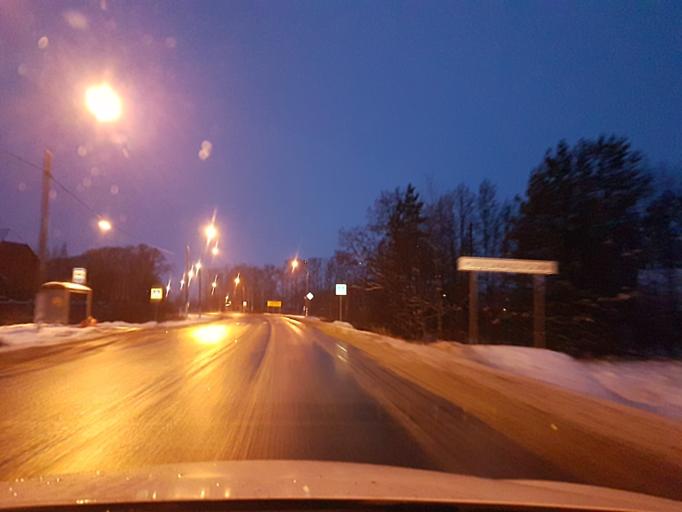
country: RU
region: Tverskaya
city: Novozavidovskiy
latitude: 56.5700
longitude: 36.4444
